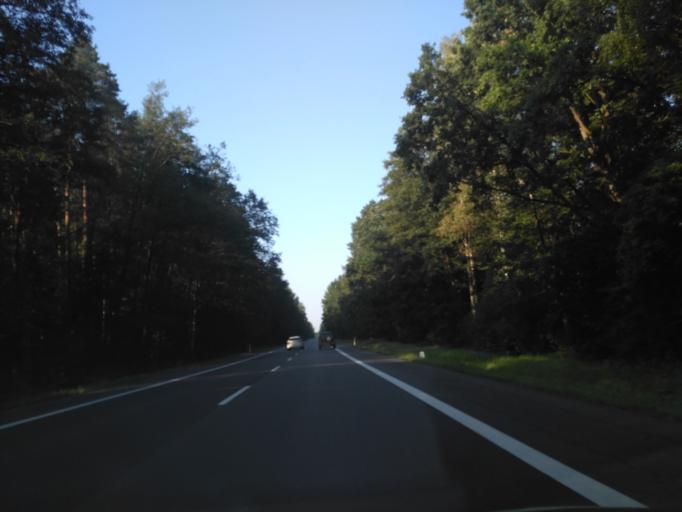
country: PL
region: Subcarpathian Voivodeship
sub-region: Powiat nizanski
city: Zarzecze
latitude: 50.5619
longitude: 22.2448
